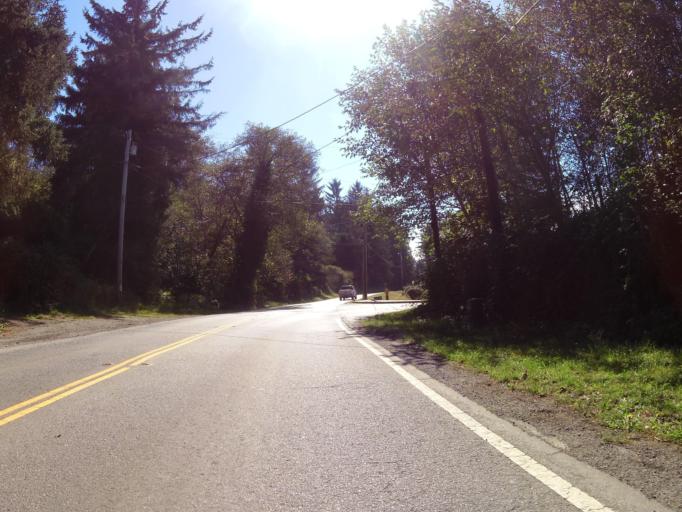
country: US
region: Oregon
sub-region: Curry County
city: Harbor
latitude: 41.9572
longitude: -124.2005
